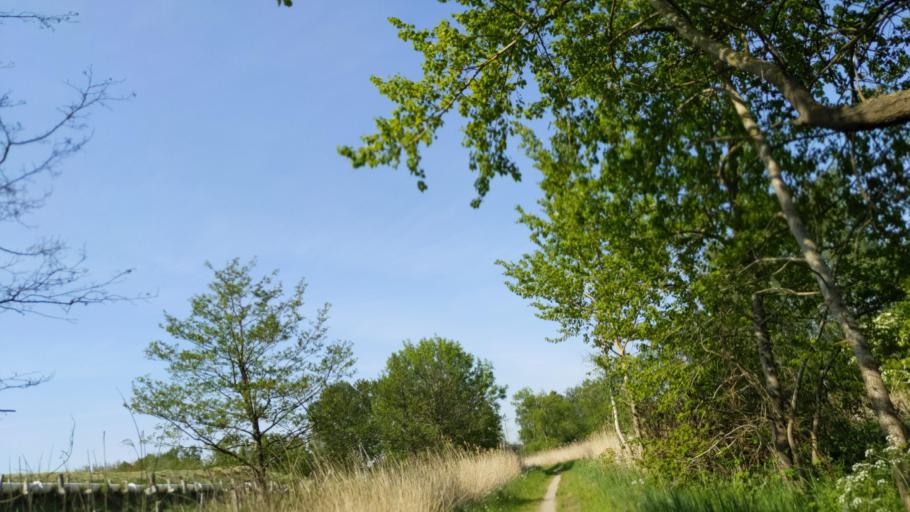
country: DE
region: Schleswig-Holstein
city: Ratekau
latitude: 53.8946
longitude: 10.7669
